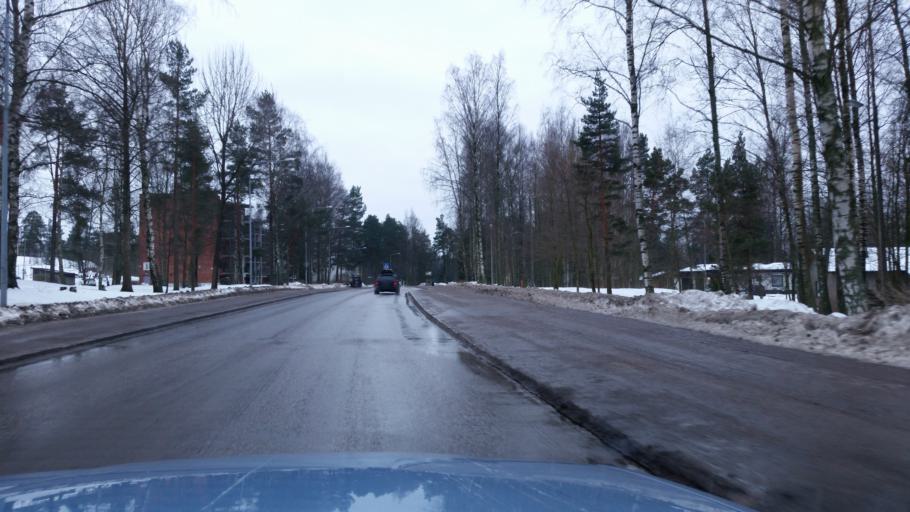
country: FI
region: Uusimaa
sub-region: Helsinki
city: Vantaa
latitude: 60.2233
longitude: 25.0578
